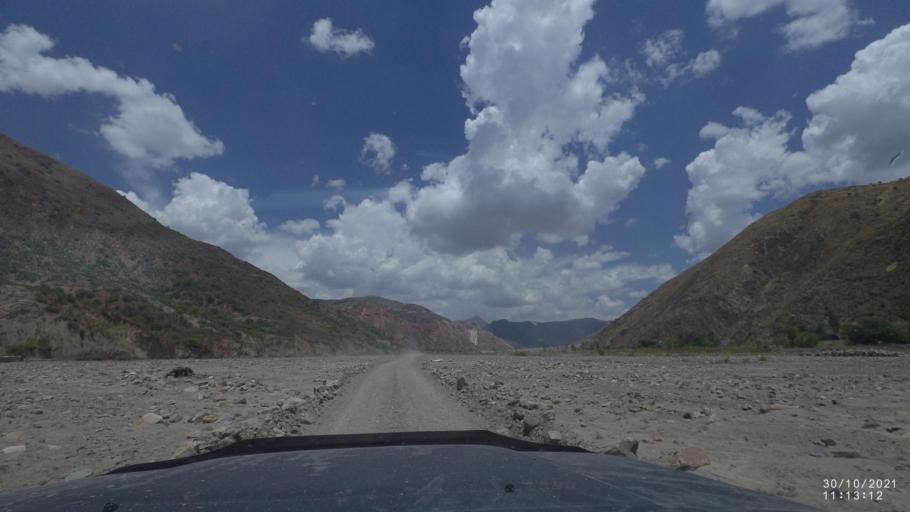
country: BO
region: Cochabamba
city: Sipe Sipe
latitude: -17.5266
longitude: -66.5747
